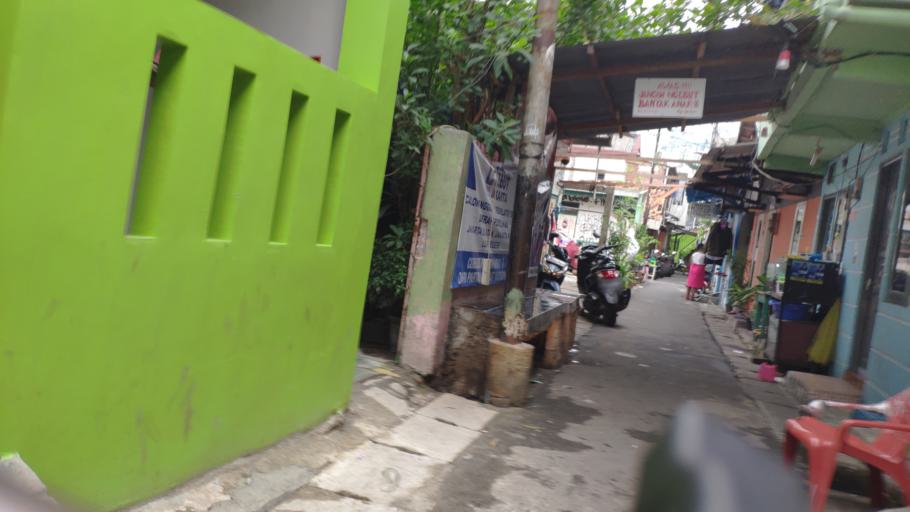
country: ID
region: Jakarta Raya
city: Jakarta
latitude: -6.2111
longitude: 106.8391
